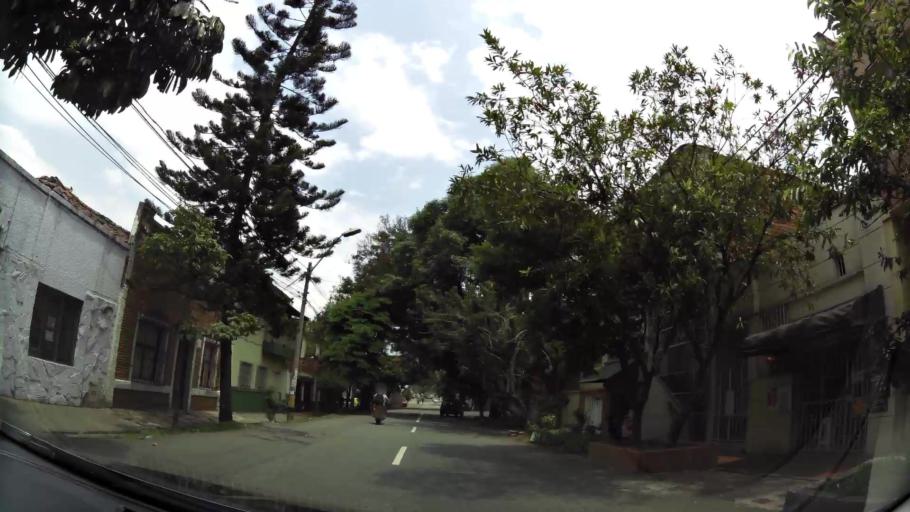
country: CO
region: Antioquia
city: Medellin
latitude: 6.2626
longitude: -75.5627
